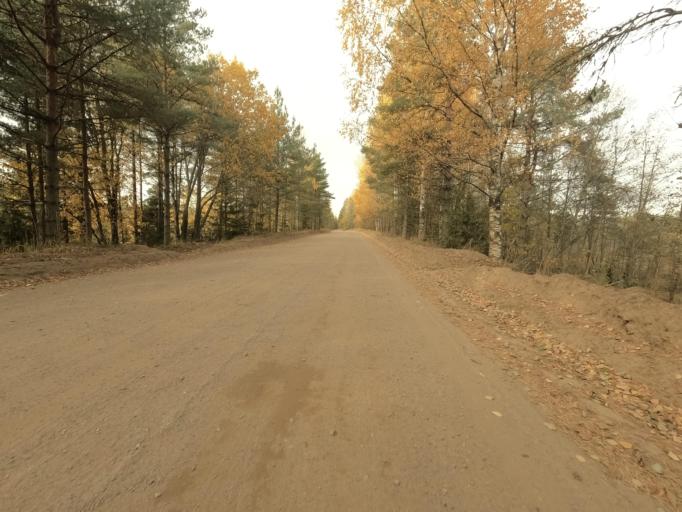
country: RU
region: Leningrad
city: Priladozhskiy
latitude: 59.6761
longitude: 31.3659
